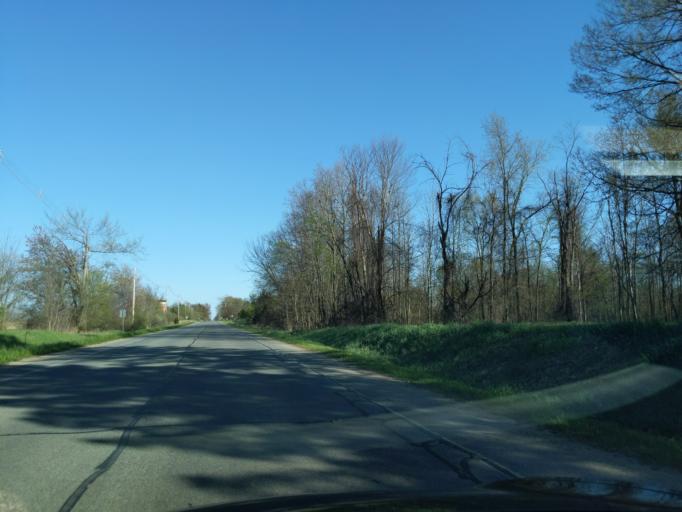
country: US
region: Michigan
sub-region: Ionia County
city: Portland
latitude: 42.8470
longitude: -84.8725
